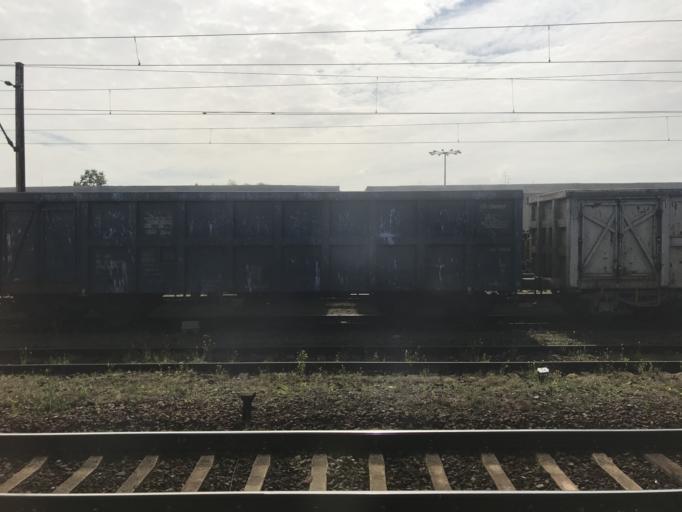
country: PL
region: Kujawsko-Pomorskie
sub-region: Powiat inowroclawski
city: Inowroclaw
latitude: 52.8019
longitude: 18.2408
